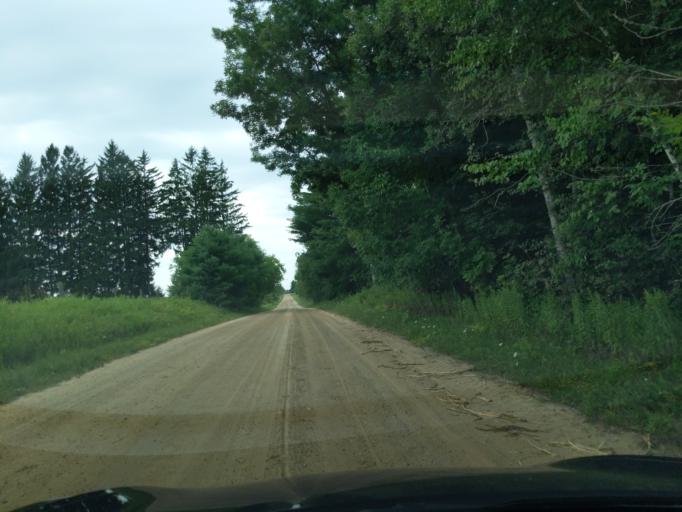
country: US
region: Michigan
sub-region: Clare County
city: Harrison
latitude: 44.0025
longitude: -84.9819
